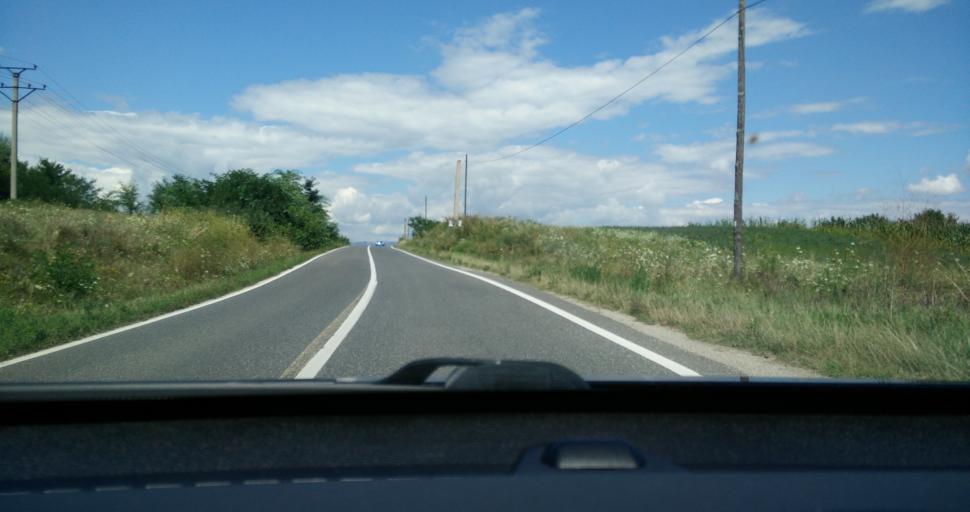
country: RO
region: Alba
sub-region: Comuna Sasciori
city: Sebesel
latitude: 45.8987
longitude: 23.5599
